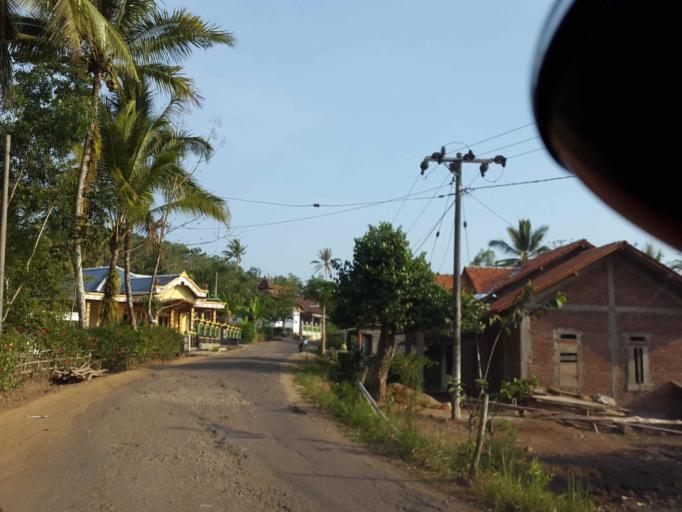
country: ID
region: East Java
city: Ploso
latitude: -8.1027
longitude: 111.0705
